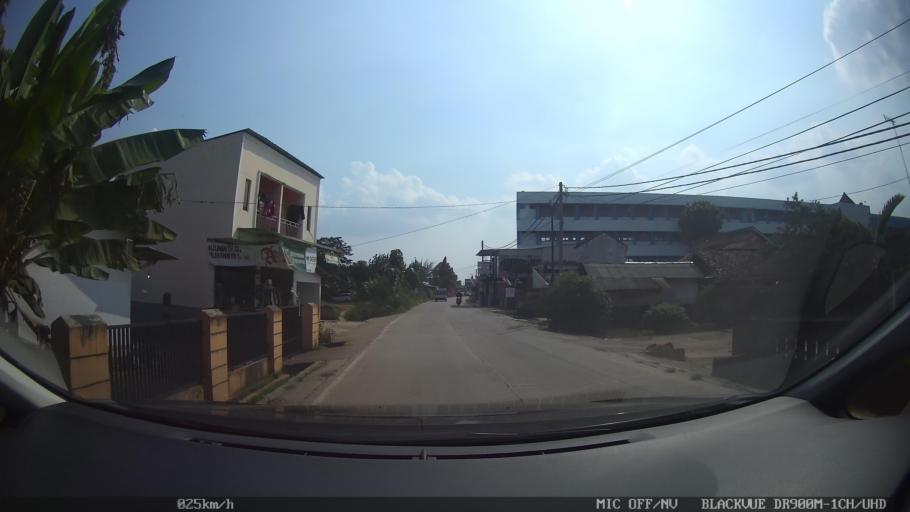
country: ID
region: Lampung
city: Natar
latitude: -5.3119
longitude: 105.1985
